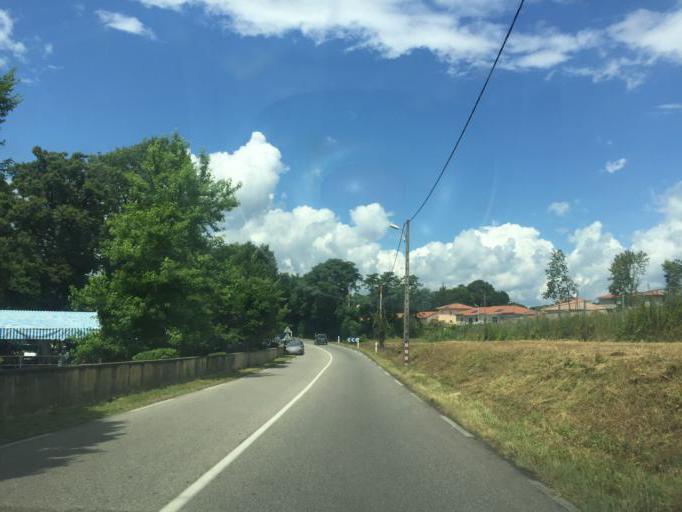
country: FR
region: Rhone-Alpes
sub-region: Departement de l'Isere
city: Charvieu-Chavagneux
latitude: 45.7512
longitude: 5.1560
